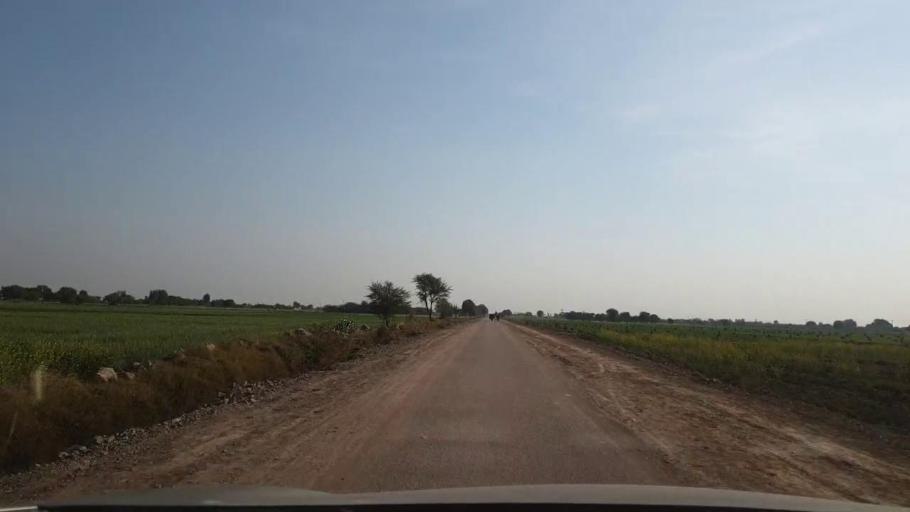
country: PK
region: Sindh
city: Berani
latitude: 25.7237
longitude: 68.8068
